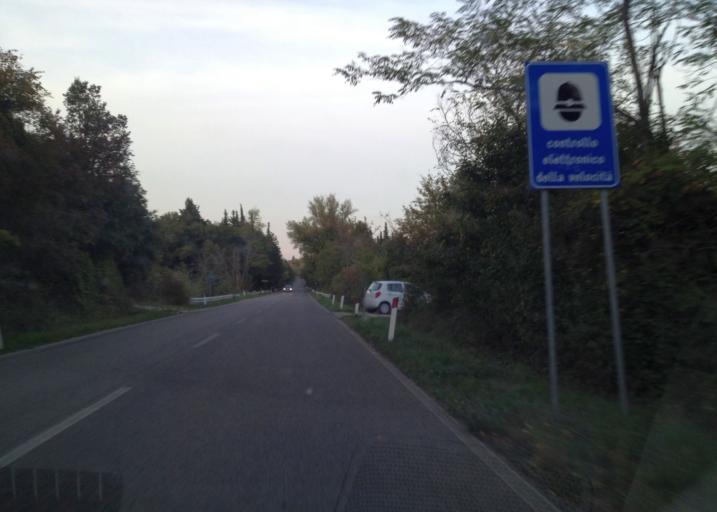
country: IT
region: Tuscany
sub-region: Provincia di Siena
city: Castellina in Chianti
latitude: 43.4835
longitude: 11.2982
